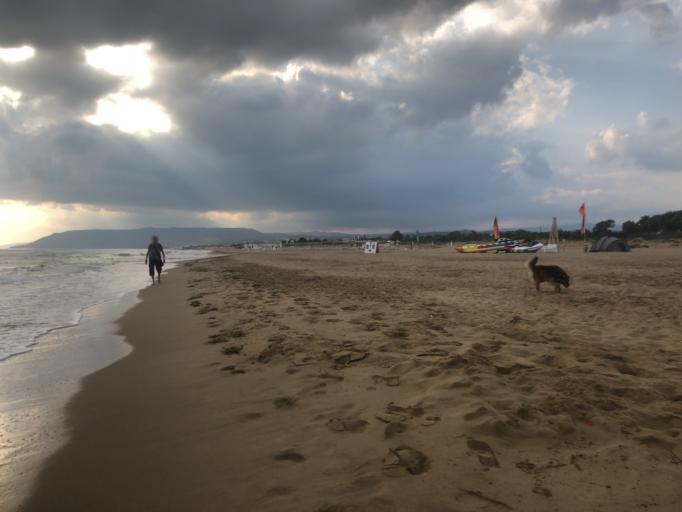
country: GR
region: Crete
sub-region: Nomos Chanias
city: Georgioupolis
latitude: 35.3565
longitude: 24.2798
